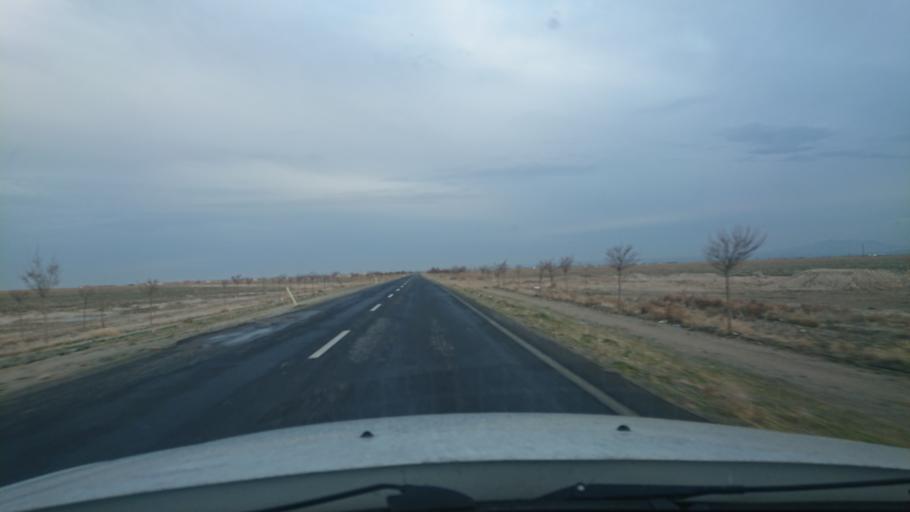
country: TR
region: Aksaray
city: Yesilova
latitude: 38.3136
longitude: 33.7538
